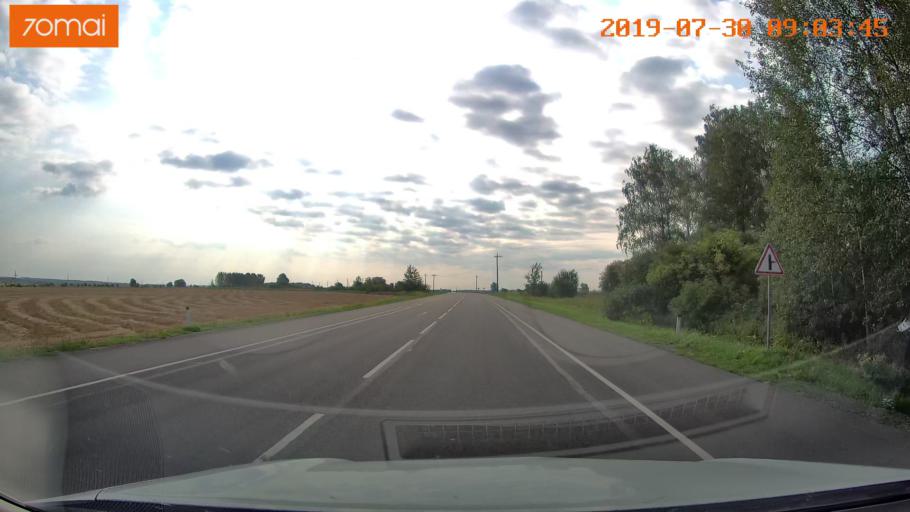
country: RU
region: Kaliningrad
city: Gusev
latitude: 54.6061
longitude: 22.2617
